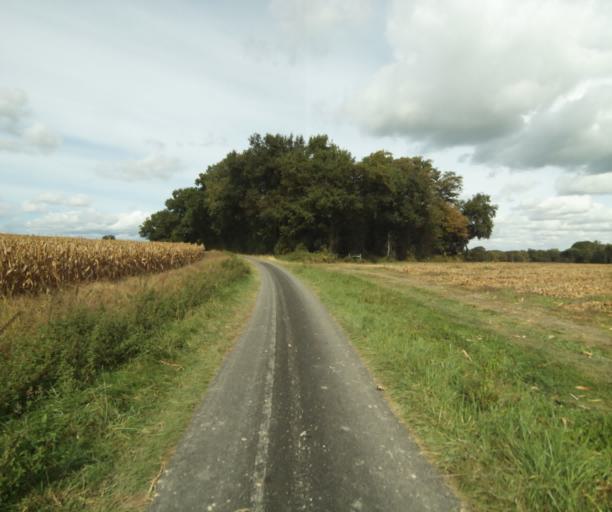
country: FR
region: Midi-Pyrenees
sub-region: Departement du Gers
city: Eauze
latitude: 43.8286
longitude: 0.1049
